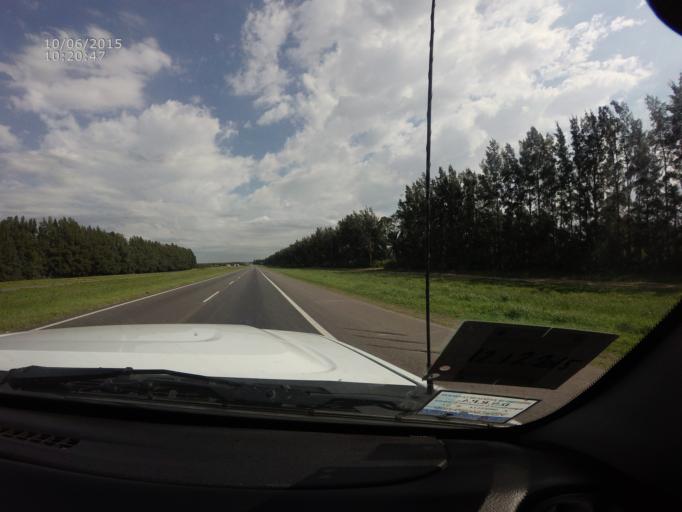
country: AR
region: Buenos Aires
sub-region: Partido de San Pedro
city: San Pedro
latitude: -33.7145
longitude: -59.8248
